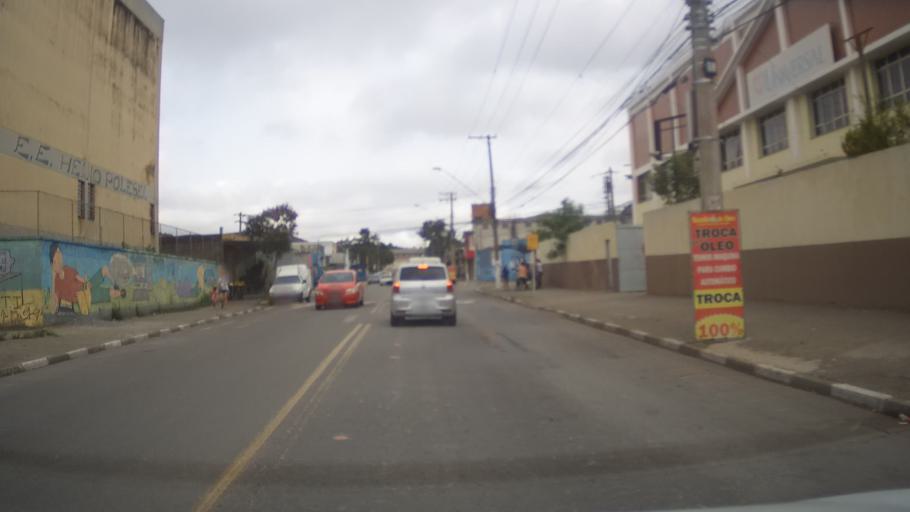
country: BR
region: Sao Paulo
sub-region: Aruja
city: Aruja
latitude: -23.4074
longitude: -46.3915
